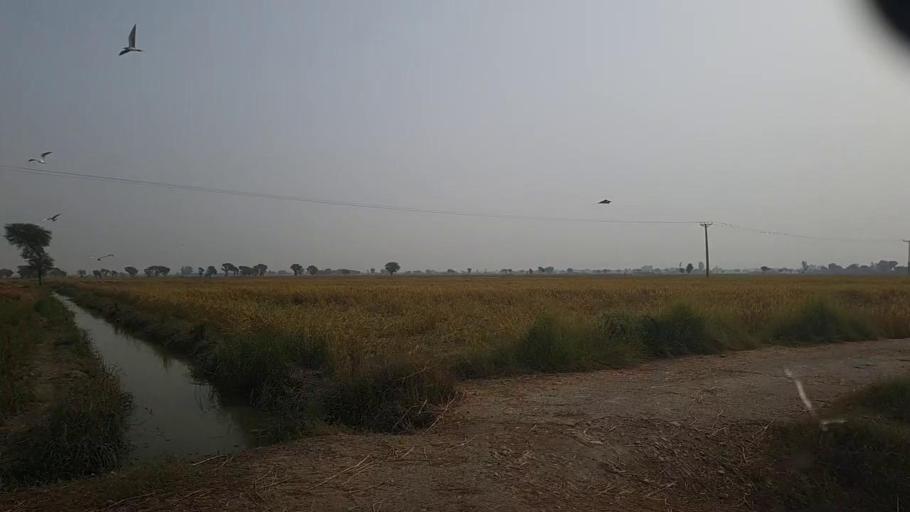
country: PK
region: Sindh
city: Kashmor
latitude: 28.3852
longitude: 69.4299
